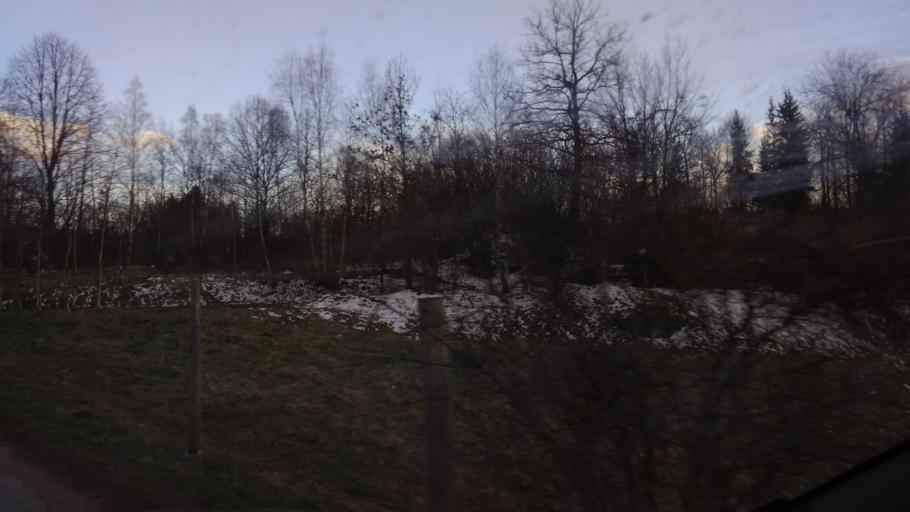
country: PL
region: Lower Silesian Voivodeship
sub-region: Powiat jeleniogorski
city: Sosnowka
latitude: 50.8486
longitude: 15.7346
